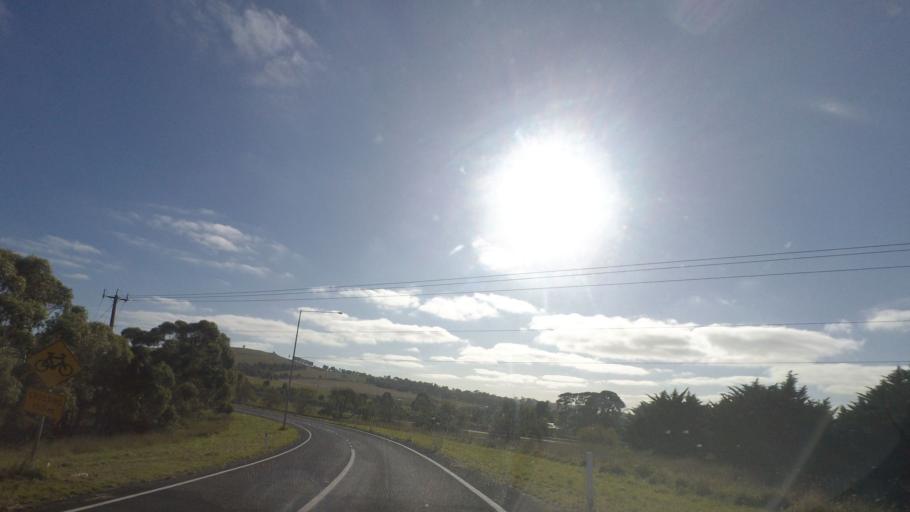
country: AU
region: Victoria
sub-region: Hume
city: Sunbury
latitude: -37.5399
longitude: 144.6419
